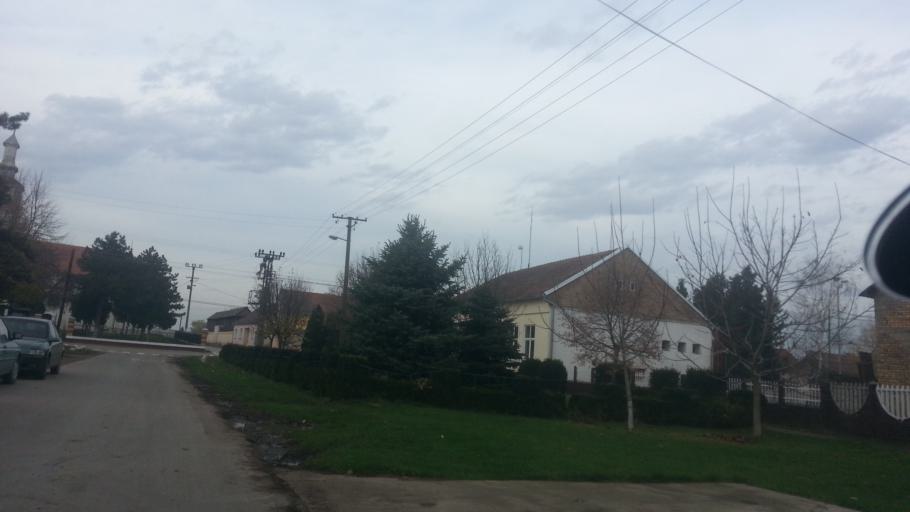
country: RS
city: Putinci
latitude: 44.9658
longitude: 19.9743
